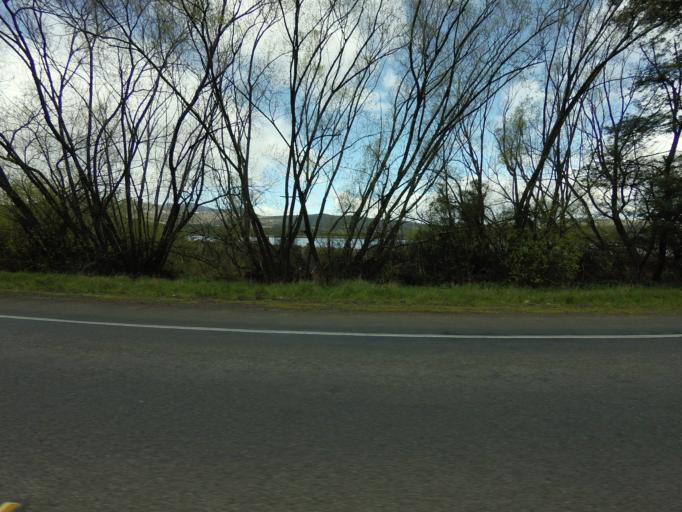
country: AU
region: Tasmania
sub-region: Huon Valley
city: Franklin
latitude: -43.1006
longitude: 147.0036
